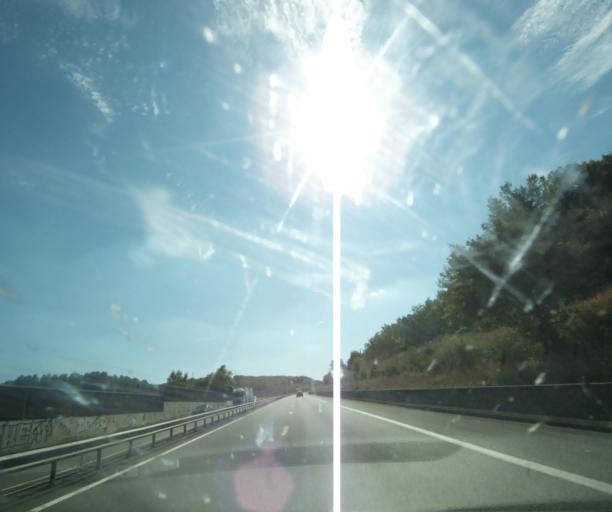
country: FR
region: Limousin
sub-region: Departement de la Correze
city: Brive-la-Gaillarde
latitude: 45.0765
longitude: 1.5125
